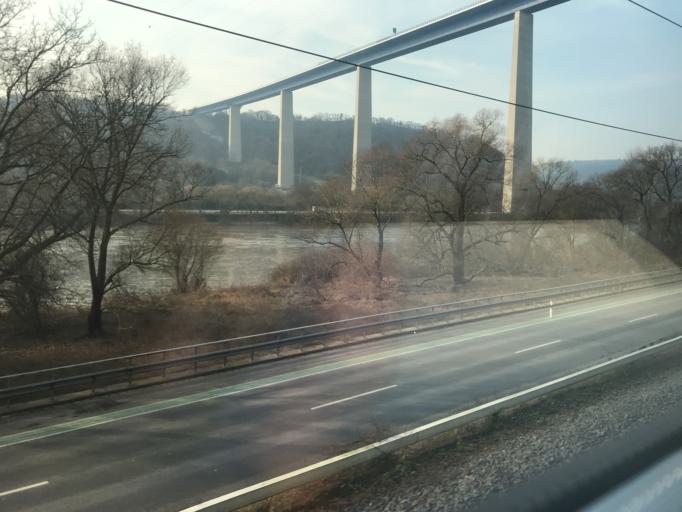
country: DE
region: Rheinland-Pfalz
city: Winningen
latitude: 50.3129
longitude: 7.4990
